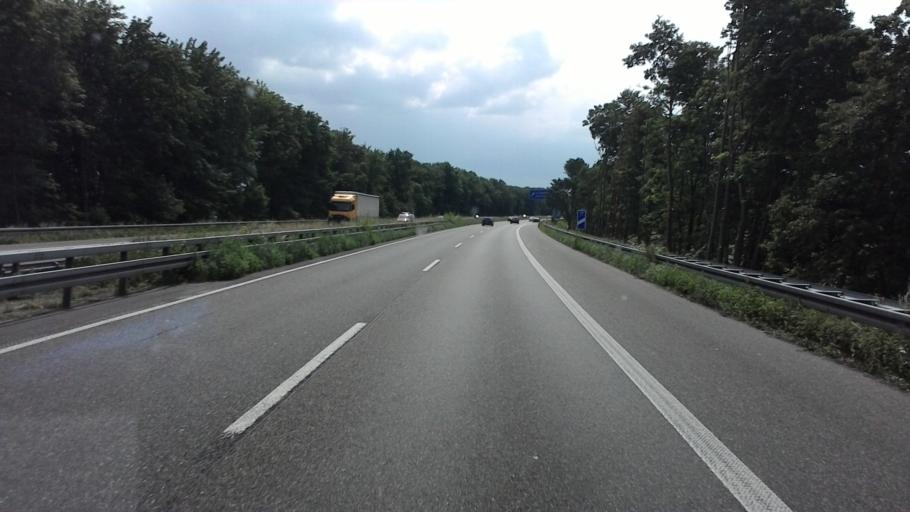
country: BE
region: Wallonia
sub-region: Province de Liege
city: Raeren
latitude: 50.7265
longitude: 6.1321
